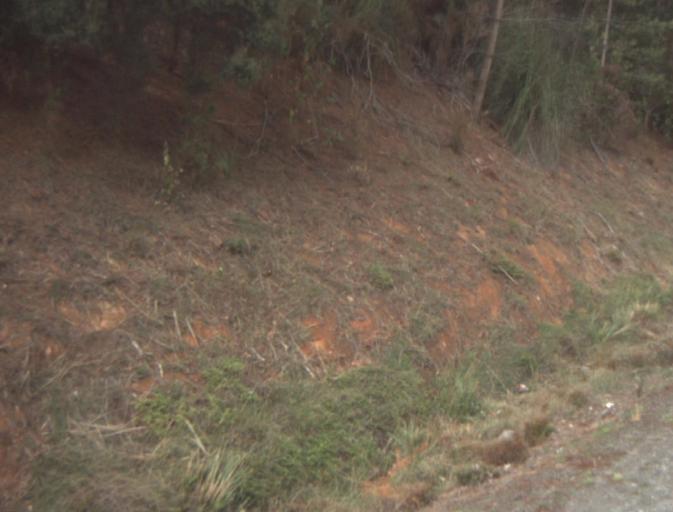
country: AU
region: Tasmania
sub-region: Launceston
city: Mayfield
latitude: -41.3009
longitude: 147.2065
